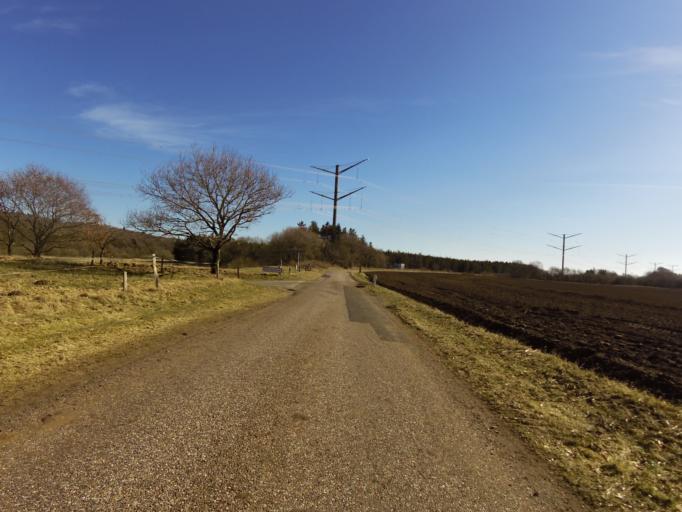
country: DK
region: South Denmark
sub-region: Tonder Kommune
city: Toftlund
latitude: 55.2247
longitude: 9.1450
